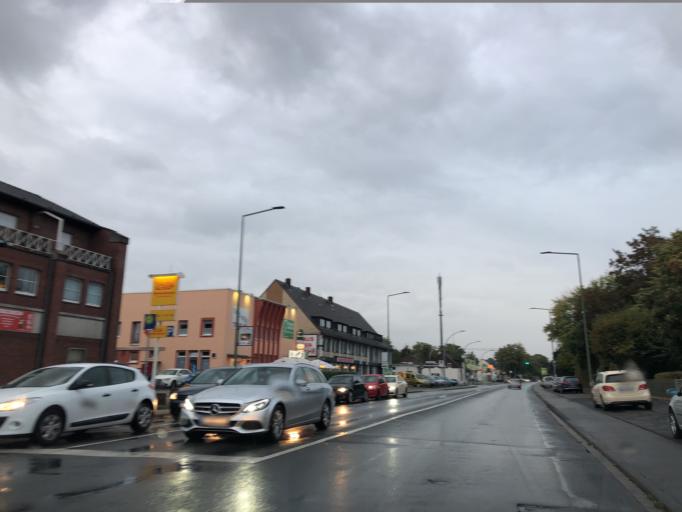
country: DE
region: North Rhine-Westphalia
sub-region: Regierungsbezirk Dusseldorf
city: Hochfeld
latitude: 51.3837
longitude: 6.7588
